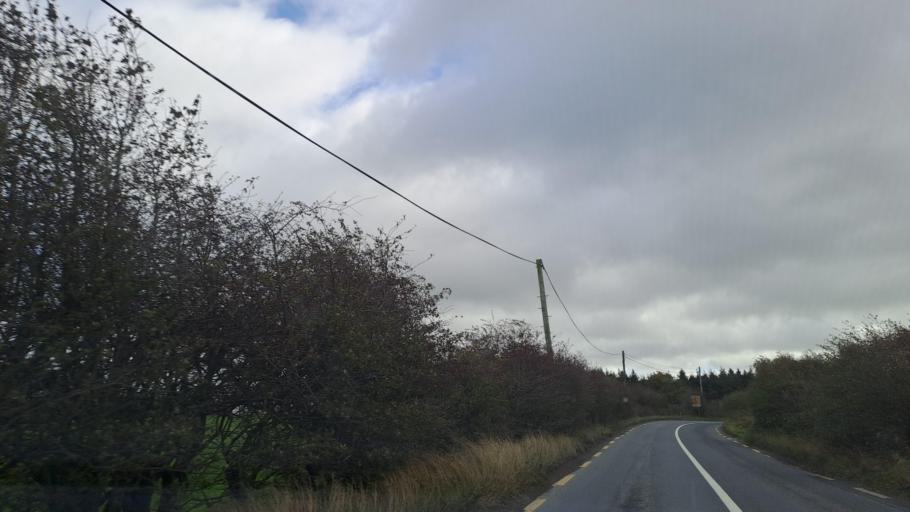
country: IE
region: Ulster
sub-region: An Cabhan
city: Kingscourt
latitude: 53.9304
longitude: -6.8825
